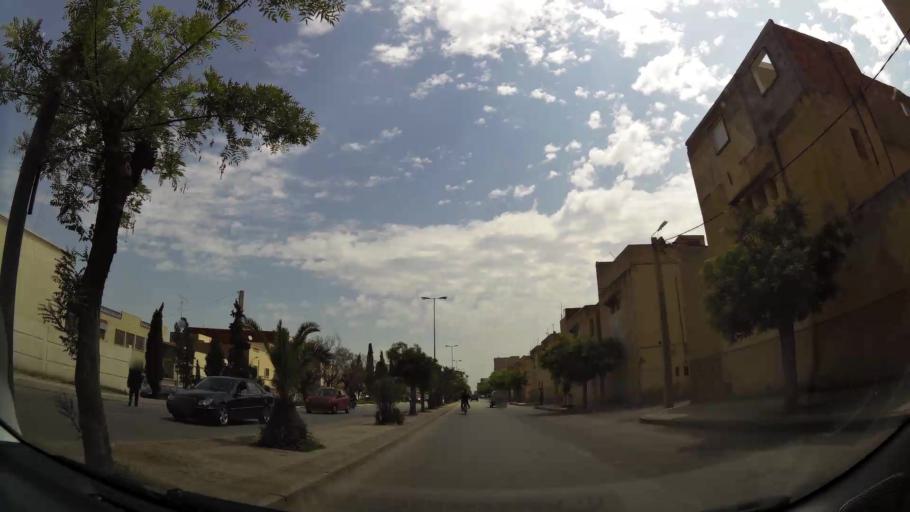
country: MA
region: Oriental
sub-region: Oujda-Angad
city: Oujda
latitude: 34.6812
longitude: -1.8879
